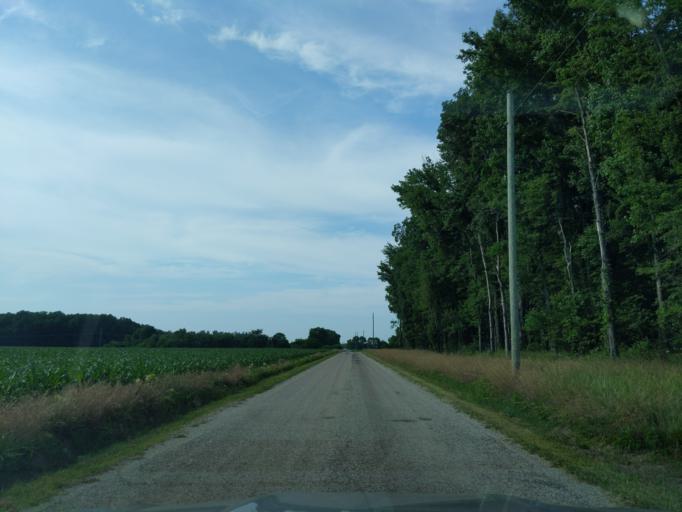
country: US
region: Indiana
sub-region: Ripley County
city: Osgood
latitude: 39.1982
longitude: -85.3892
